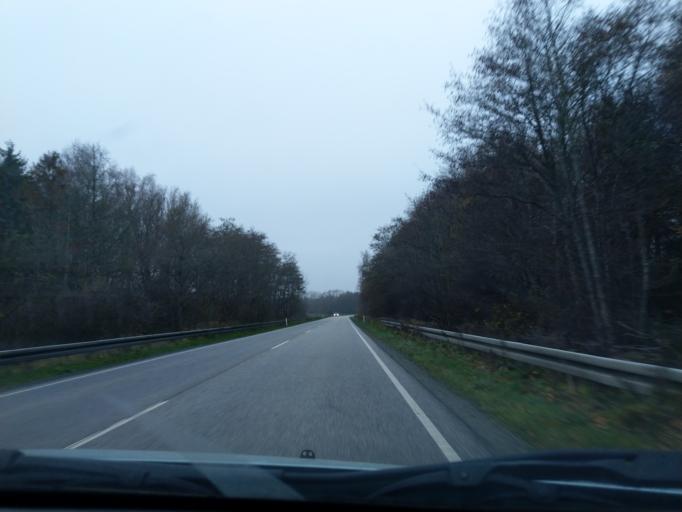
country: DK
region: Zealand
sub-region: Vordingborg Kommune
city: Praesto
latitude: 55.1125
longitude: 12.0439
